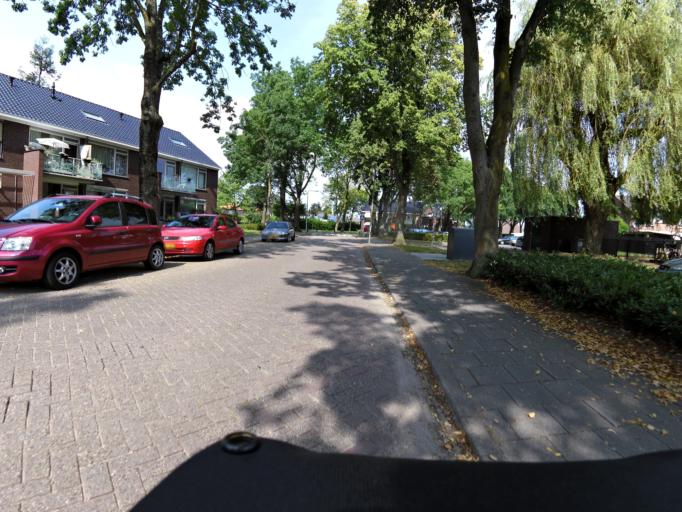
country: NL
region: South Holland
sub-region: Gemeente Binnenmaas
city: Heinenoord
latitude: 51.8266
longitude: 4.4785
